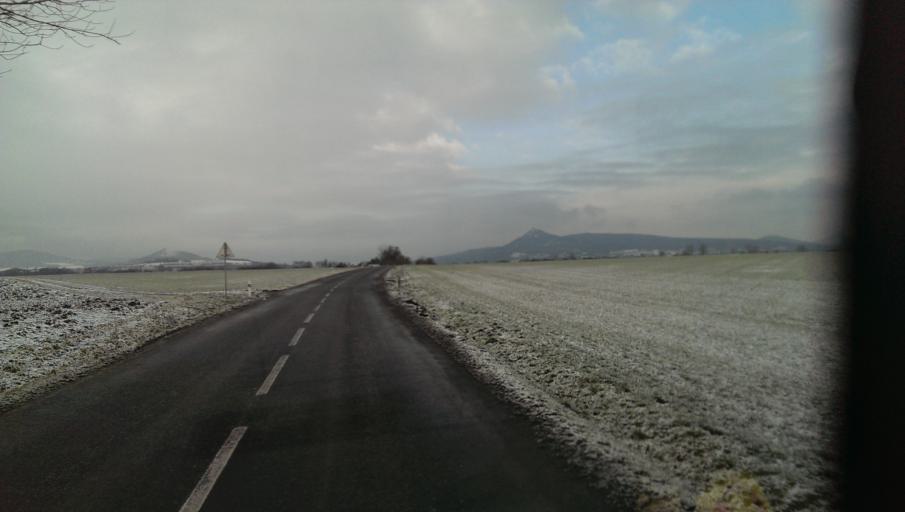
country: CZ
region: Ustecky
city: Trebenice
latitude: 50.4553
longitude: 13.9992
